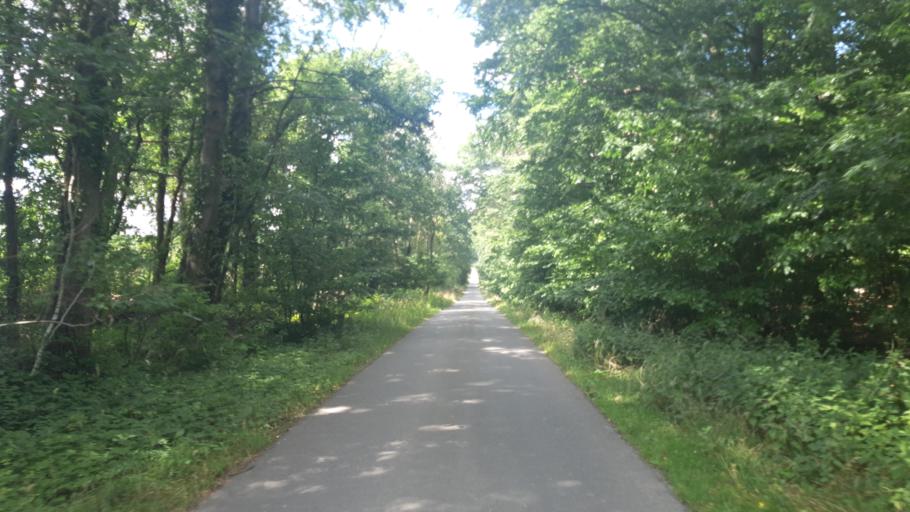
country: DE
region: Lower Saxony
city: Tosterglope
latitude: 53.2012
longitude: 10.7955
